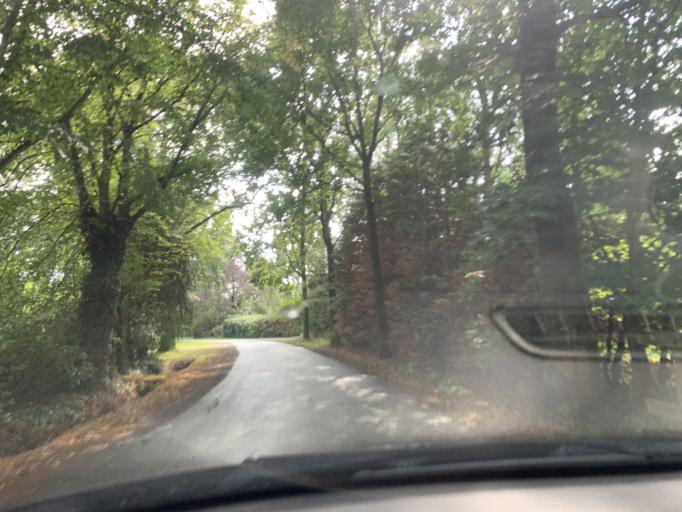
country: DE
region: Lower Saxony
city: Westerstede
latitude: 53.2668
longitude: 7.9001
